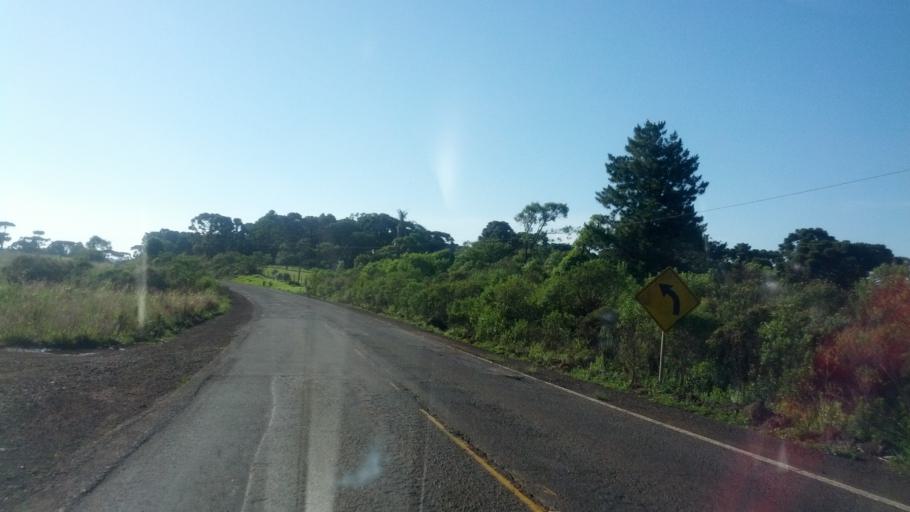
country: BR
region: Santa Catarina
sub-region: Lages
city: Lages
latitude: -27.9228
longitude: -50.5643
